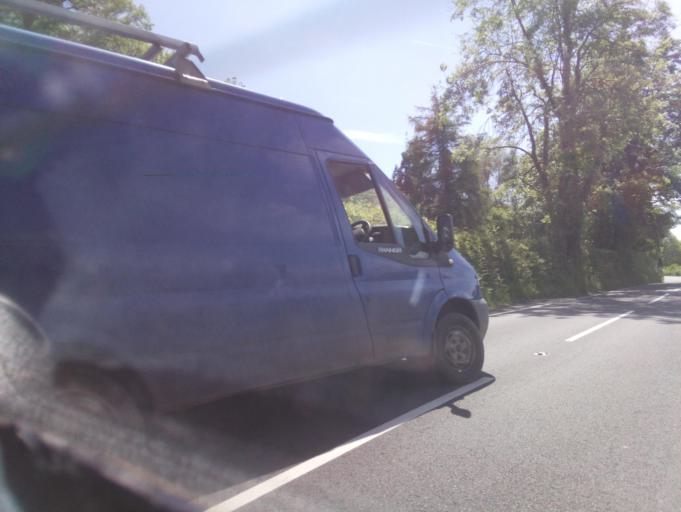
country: GB
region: Wales
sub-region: Monmouthshire
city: Mitchel Troy
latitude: 51.7801
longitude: -2.7266
